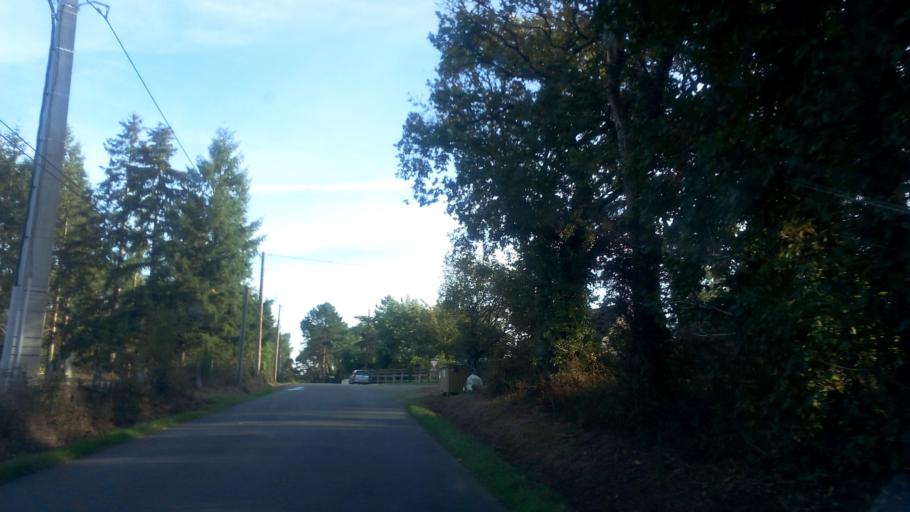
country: FR
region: Brittany
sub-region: Departement du Morbihan
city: Saint-Perreux
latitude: 47.6823
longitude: -2.0919
